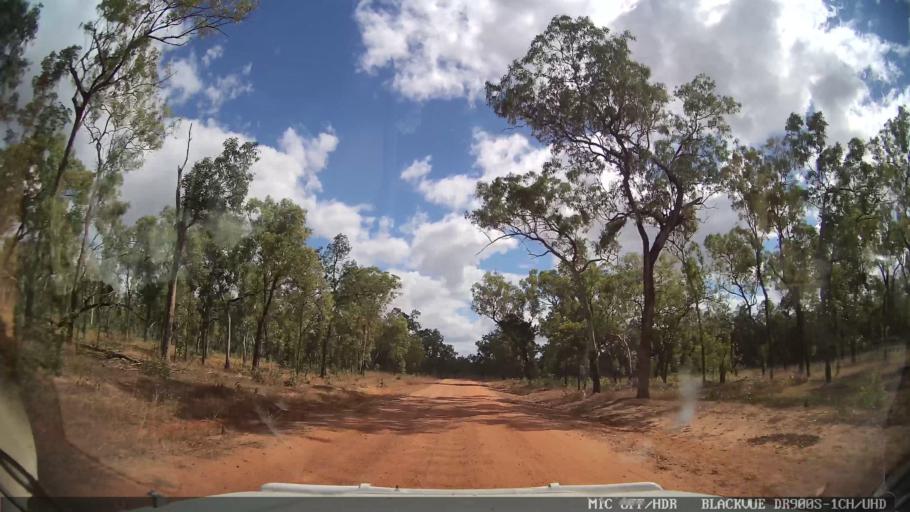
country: AU
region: Queensland
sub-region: Cook
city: Cooktown
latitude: -15.3519
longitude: 144.4627
